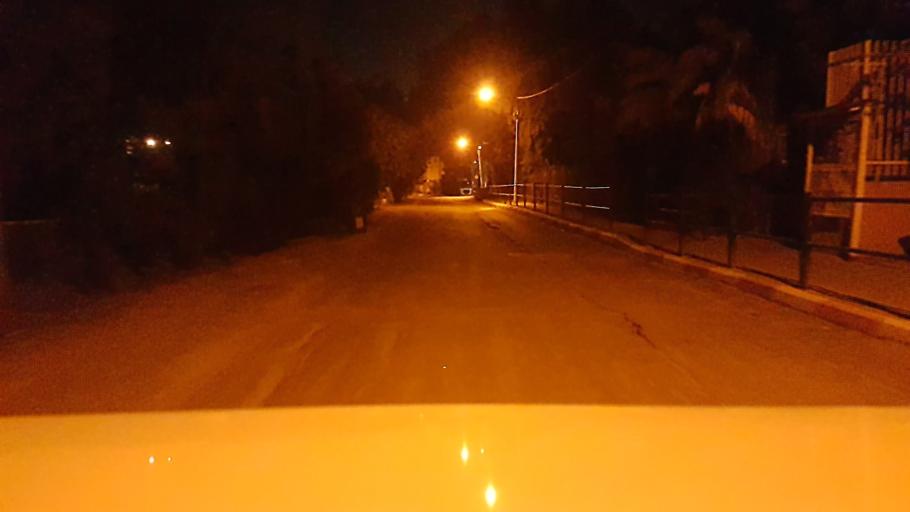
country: IL
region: Central District
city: Nehalim
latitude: 32.0767
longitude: 34.9264
